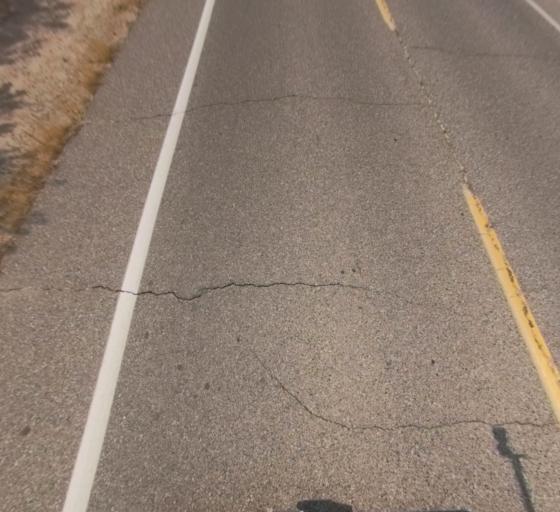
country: US
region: California
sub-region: Madera County
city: Fairmead
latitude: 37.0639
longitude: -120.1470
